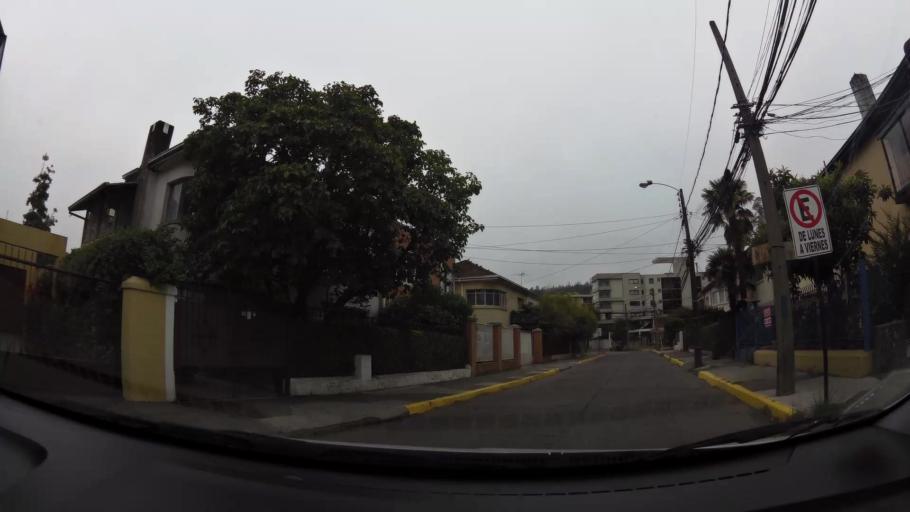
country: CL
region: Biobio
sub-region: Provincia de Concepcion
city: Concepcion
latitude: -36.8229
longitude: -73.0356
